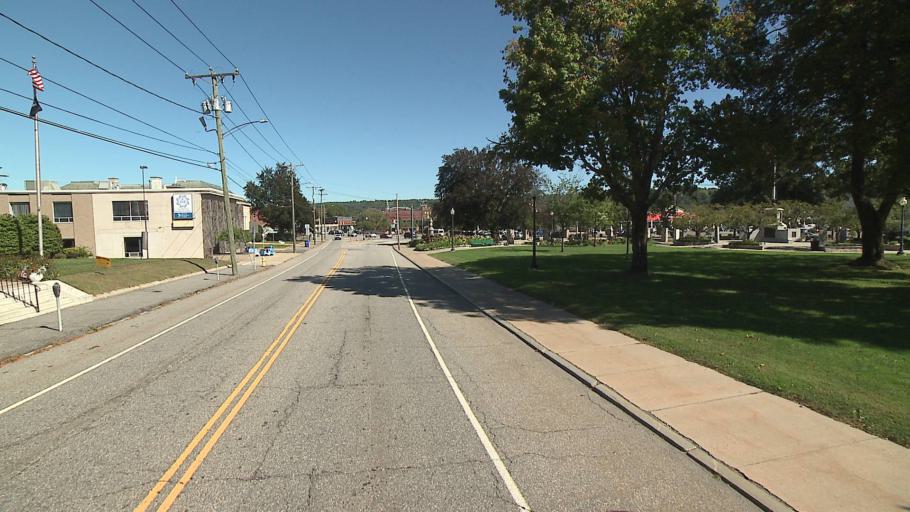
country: US
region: Connecticut
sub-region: Litchfield County
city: Torrington
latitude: 41.7991
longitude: -73.1225
